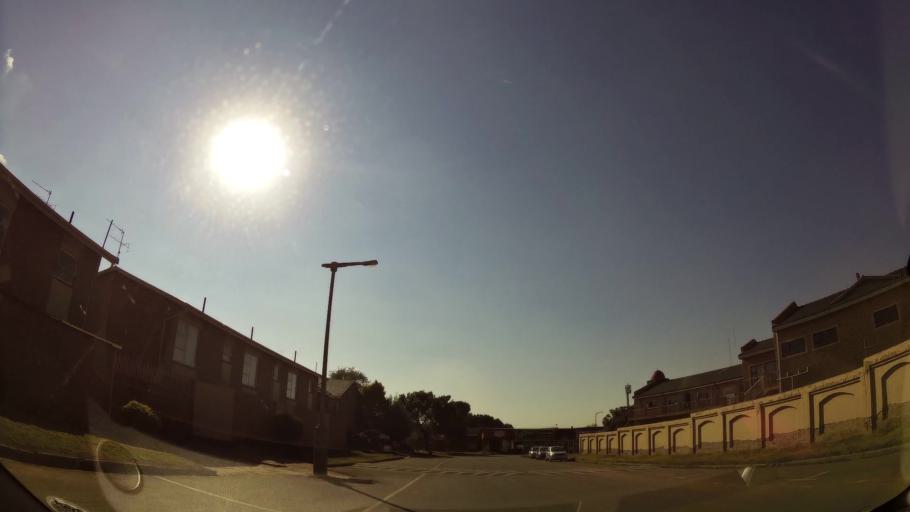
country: ZA
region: Gauteng
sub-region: Ekurhuleni Metropolitan Municipality
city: Benoni
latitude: -26.1448
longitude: 28.3422
